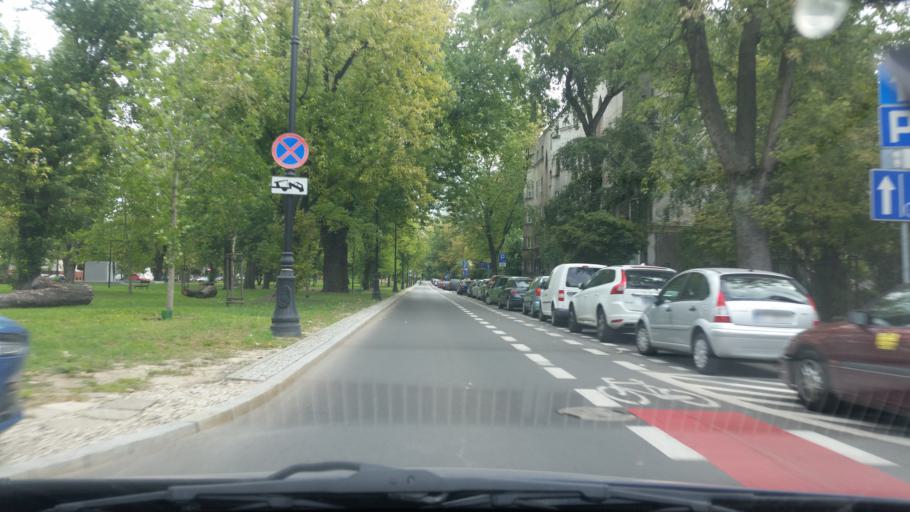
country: PL
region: Masovian Voivodeship
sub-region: Warszawa
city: Zoliborz
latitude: 52.2633
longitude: 20.9846
